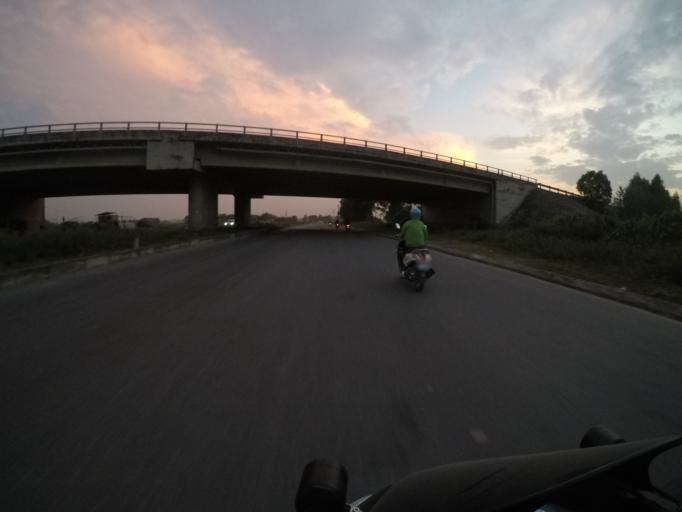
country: VN
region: Vinh Phuc
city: Phuc Yen
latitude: 21.2566
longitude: 105.7228
